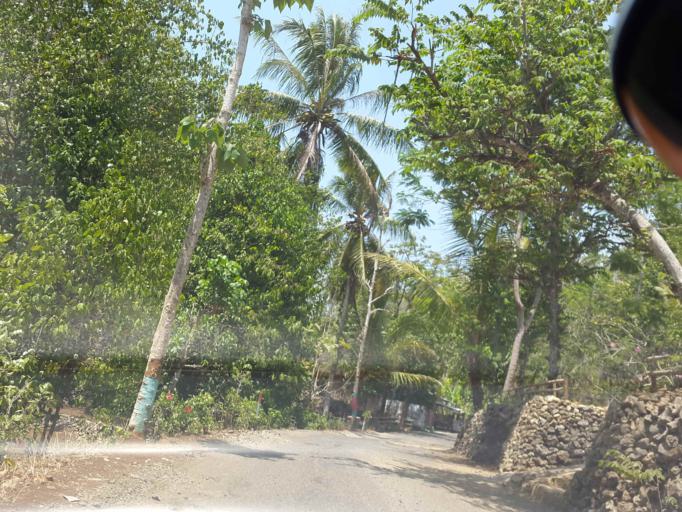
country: ID
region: East Java
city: Krajan
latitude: -8.2155
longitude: 110.9952
